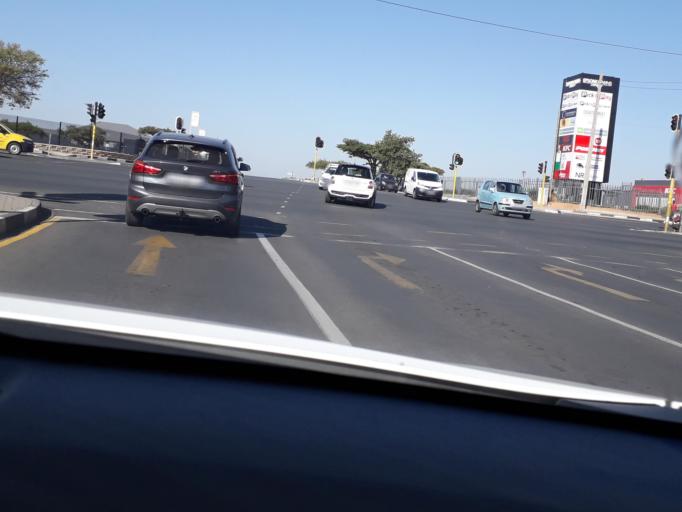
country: ZA
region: Gauteng
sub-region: City of Johannesburg Metropolitan Municipality
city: Diepsloot
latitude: -26.0425
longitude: 28.0161
